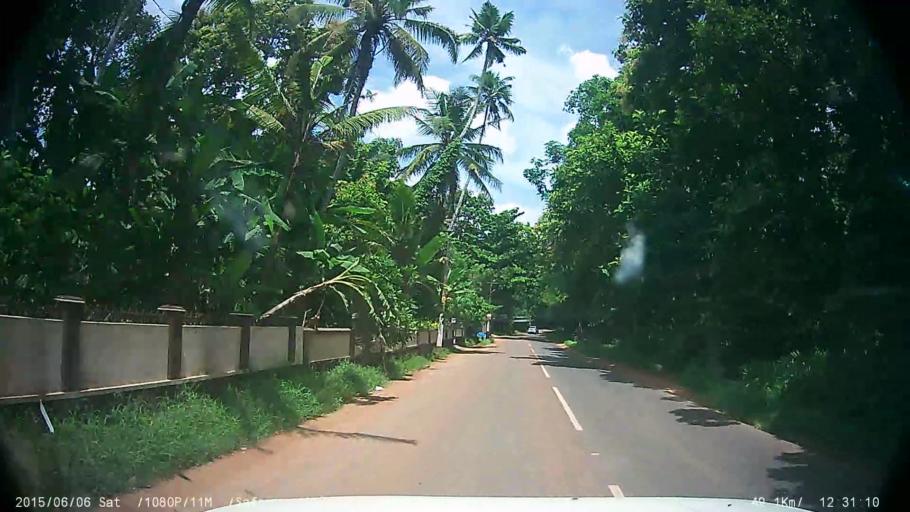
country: IN
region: Kerala
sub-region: Kottayam
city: Kottayam
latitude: 9.6191
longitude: 76.6049
